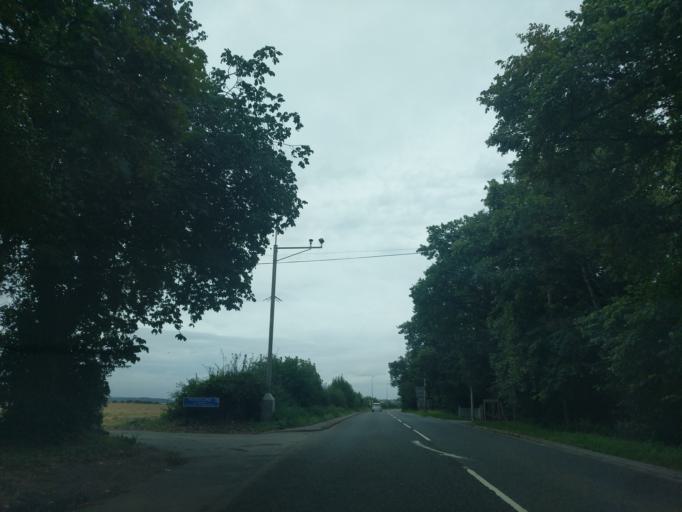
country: GB
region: England
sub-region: Lincolnshire
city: Barrowby
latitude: 52.9183
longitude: -0.6763
